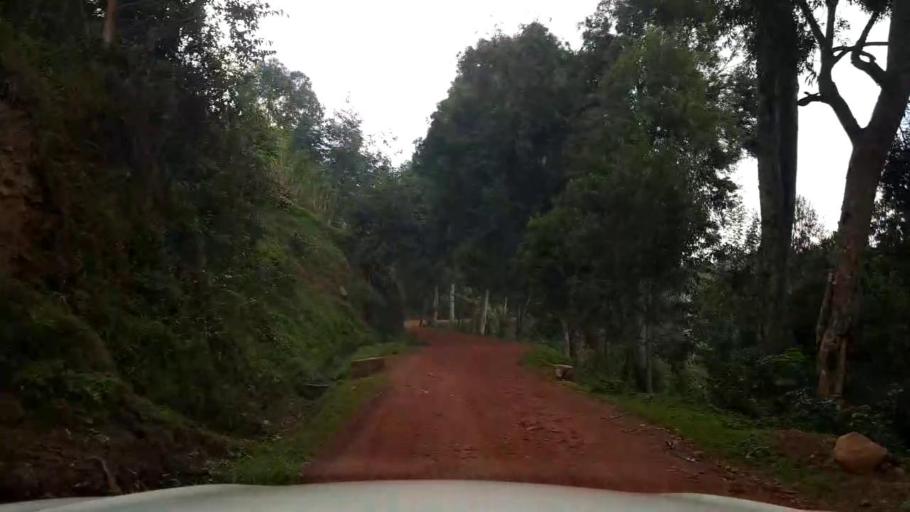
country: UG
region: Western Region
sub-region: Kisoro District
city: Kisoro
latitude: -1.4020
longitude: 29.8011
